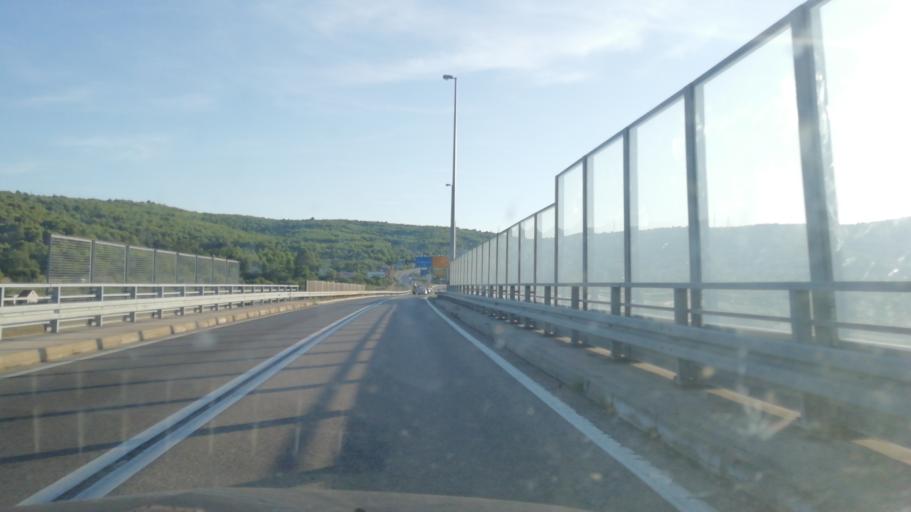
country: HR
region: Sibensko-Kniniska
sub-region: Grad Sibenik
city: Sibenik
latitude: 43.7382
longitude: 15.9365
